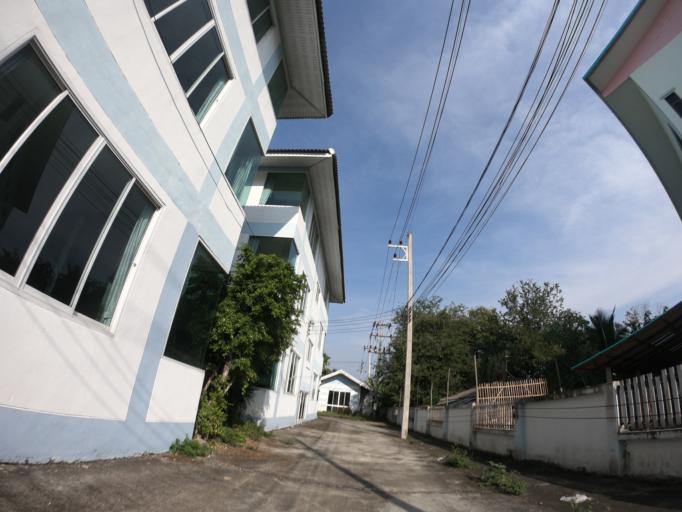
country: TH
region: Chiang Mai
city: Chiang Mai
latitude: 18.8279
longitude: 98.9916
